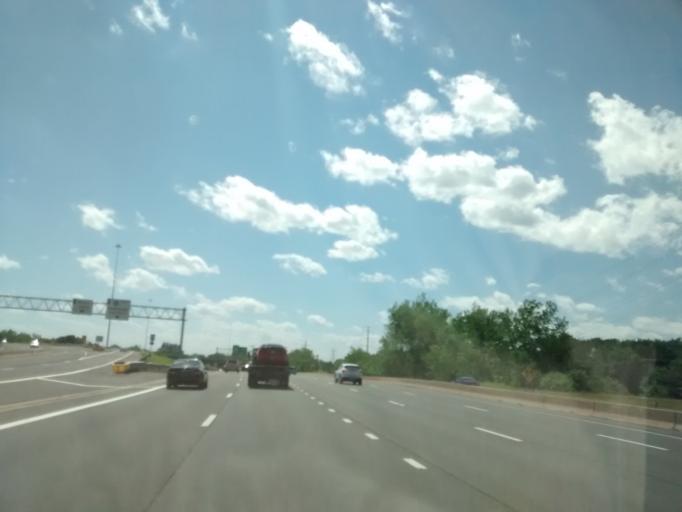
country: US
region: Connecticut
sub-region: Hartford County
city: East Hartford
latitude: 41.7653
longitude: -72.6273
